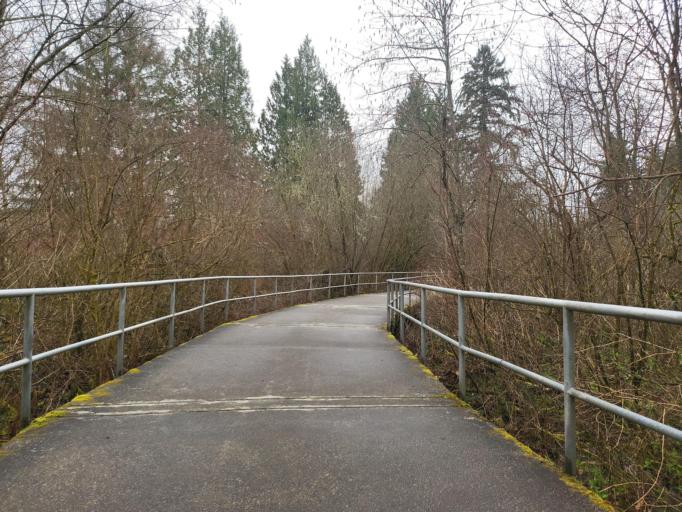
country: US
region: Washington
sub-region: King County
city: East Hill-Meridian
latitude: 47.4183
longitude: -122.1606
